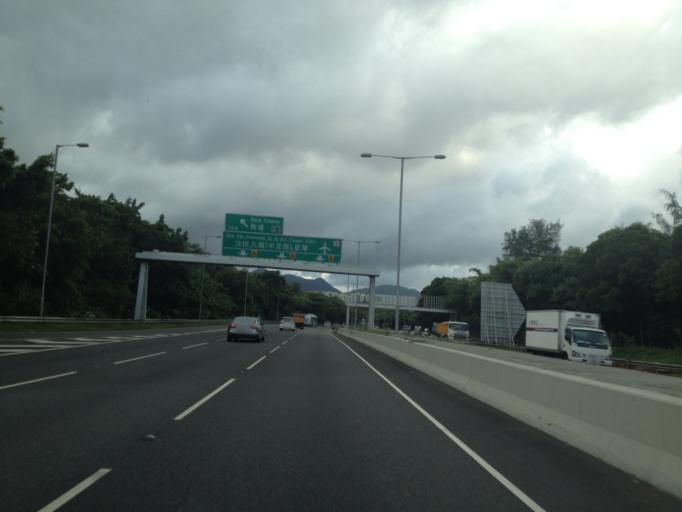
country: HK
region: Sha Tin
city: Sha Tin
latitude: 22.4104
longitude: 114.2122
